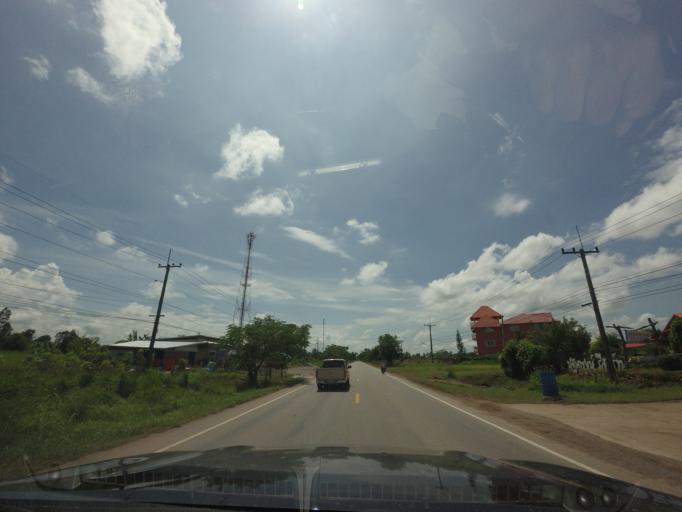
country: TH
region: Nong Khai
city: Pho Tak
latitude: 17.7712
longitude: 102.3961
